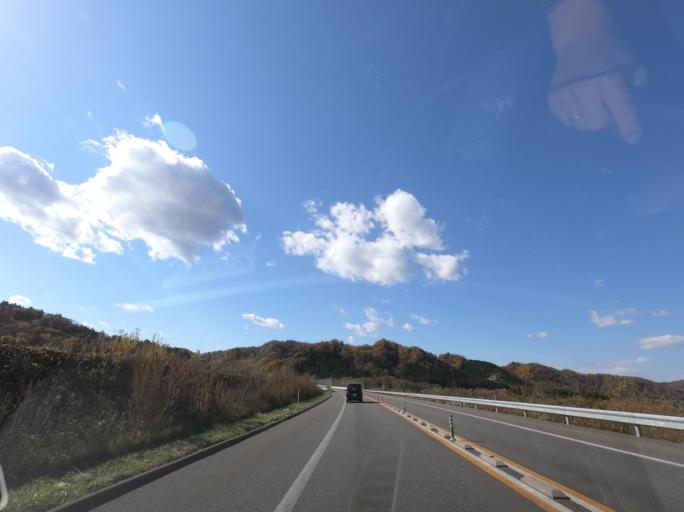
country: JP
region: Hokkaido
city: Kushiro
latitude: 43.0885
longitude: 143.9222
